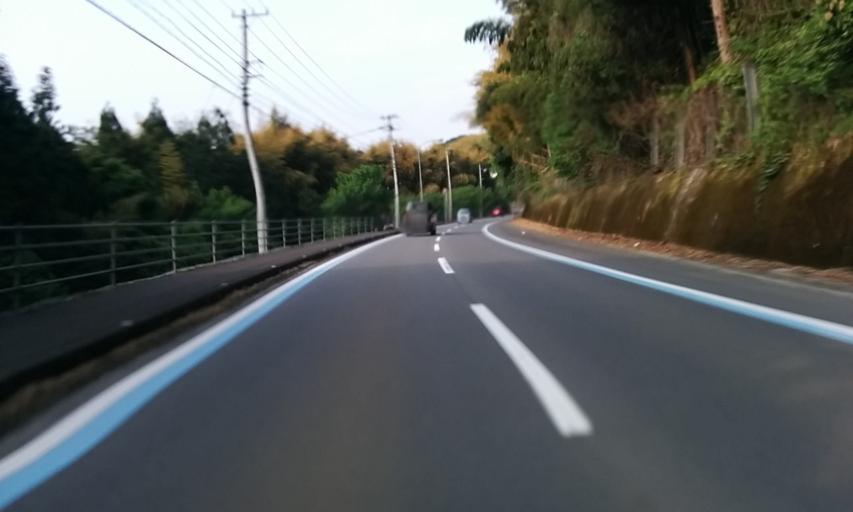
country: JP
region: Ehime
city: Saijo
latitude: 33.8811
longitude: 133.1781
